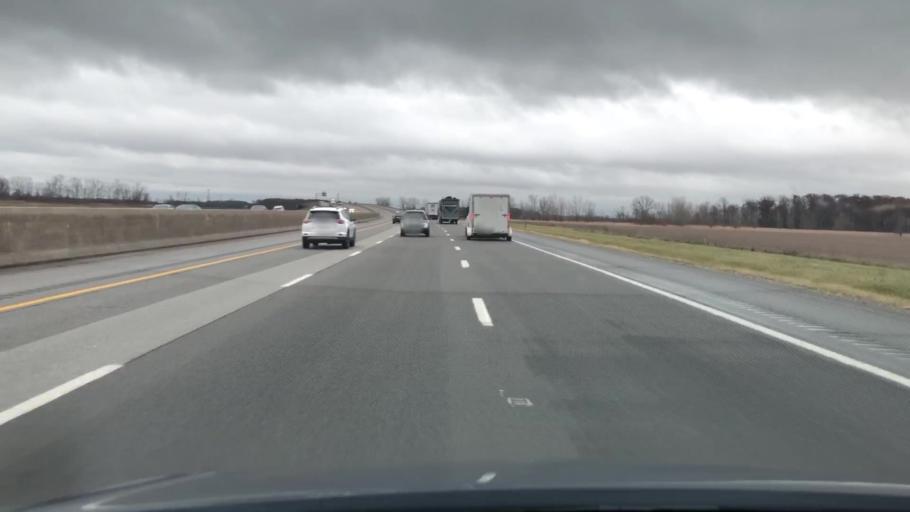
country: US
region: Ohio
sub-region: Wood County
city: Millbury
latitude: 41.5134
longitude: -83.4303
